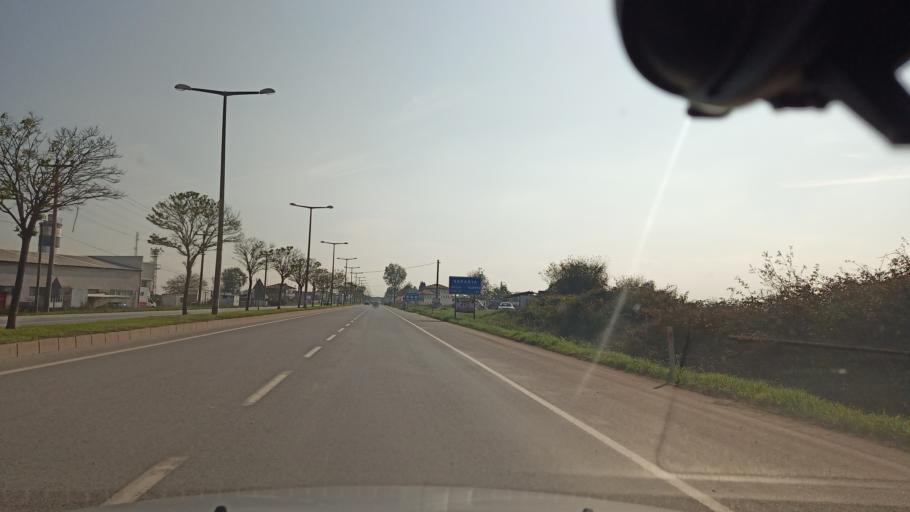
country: TR
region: Sakarya
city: Adapazari
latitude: 40.8200
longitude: 30.3981
